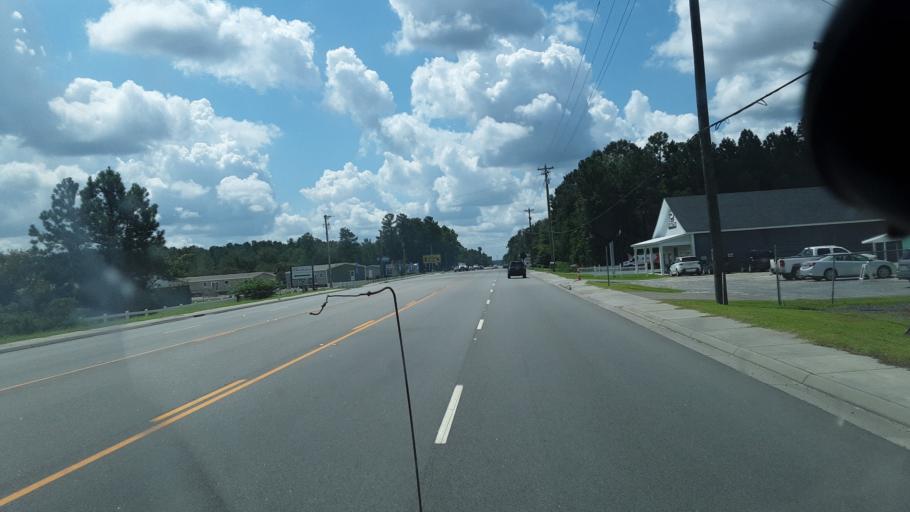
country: US
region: South Carolina
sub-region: Berkeley County
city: Sangaree
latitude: 33.1040
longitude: -80.0754
